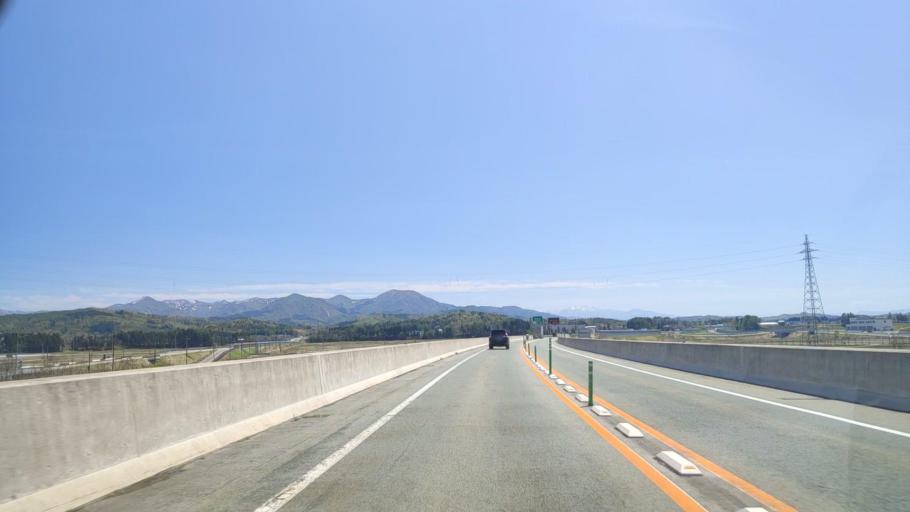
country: JP
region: Yamagata
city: Obanazawa
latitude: 38.6124
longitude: 140.3880
